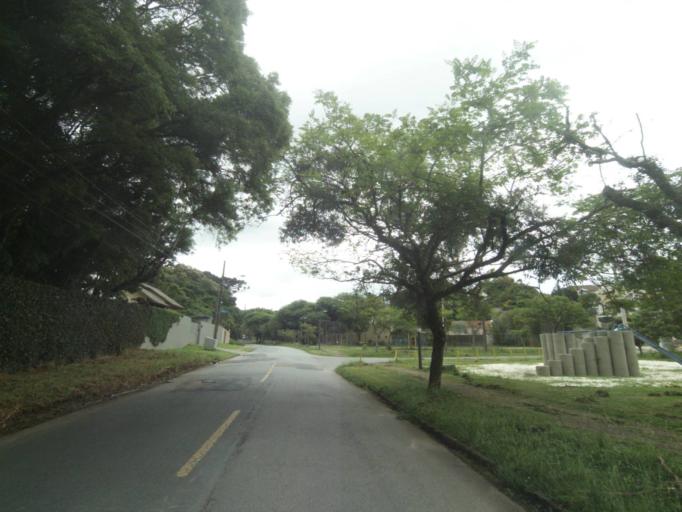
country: BR
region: Parana
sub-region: Curitiba
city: Curitiba
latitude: -25.3927
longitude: -49.2753
